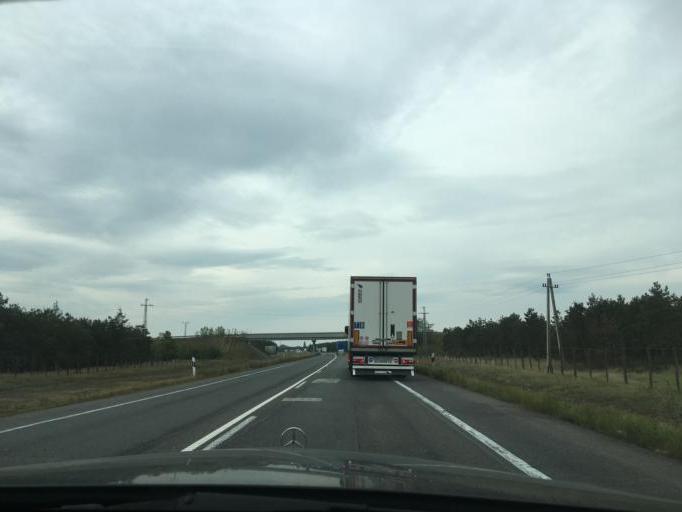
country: HU
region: Gyor-Moson-Sopron
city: Rajka
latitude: 47.9590
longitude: 17.1694
